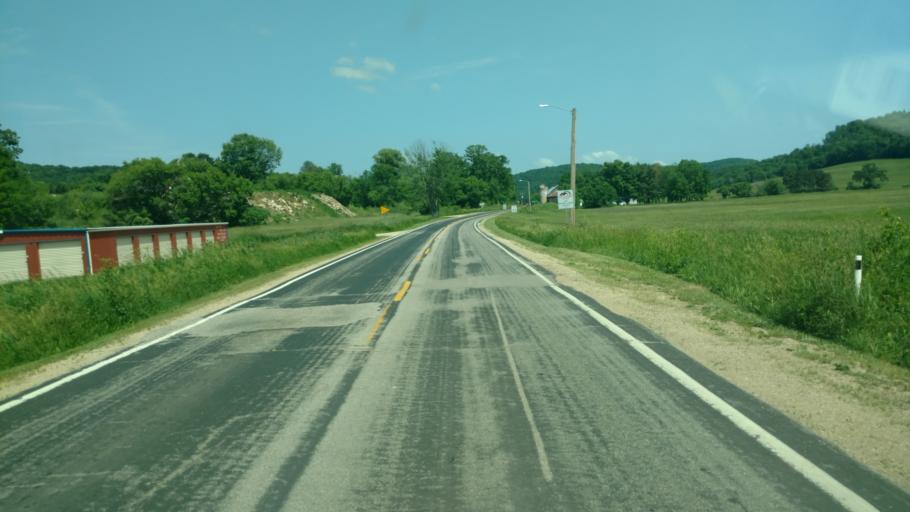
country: US
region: Wisconsin
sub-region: Monroe County
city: Cashton
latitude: 43.5743
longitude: -90.6303
